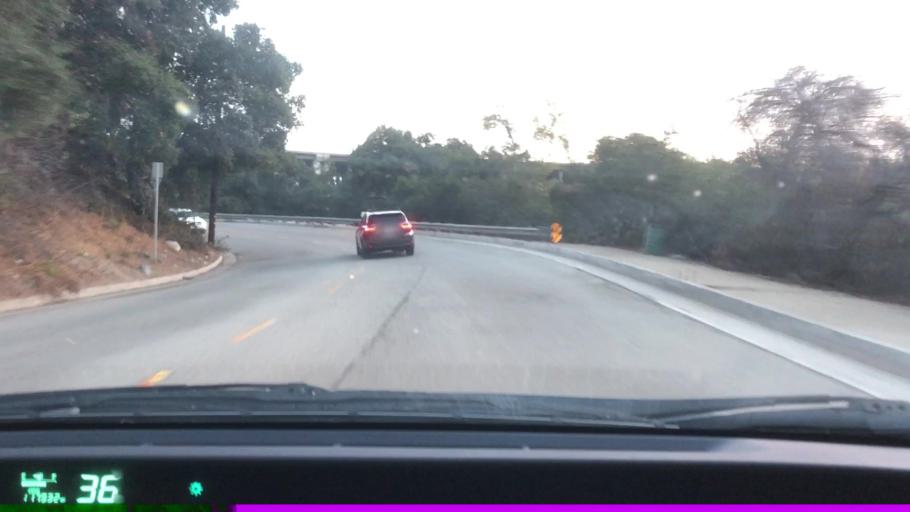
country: US
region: California
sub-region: Los Angeles County
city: Pasadena
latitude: 34.1482
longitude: -118.1654
